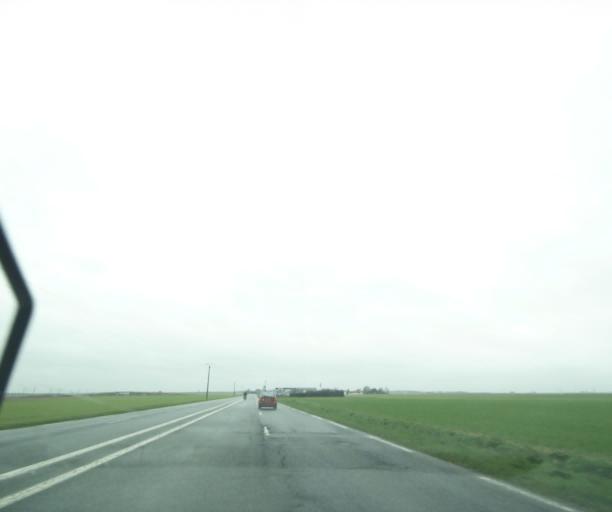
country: FR
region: Centre
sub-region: Departement du Loiret
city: Artenay
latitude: 48.0608
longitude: 1.8767
